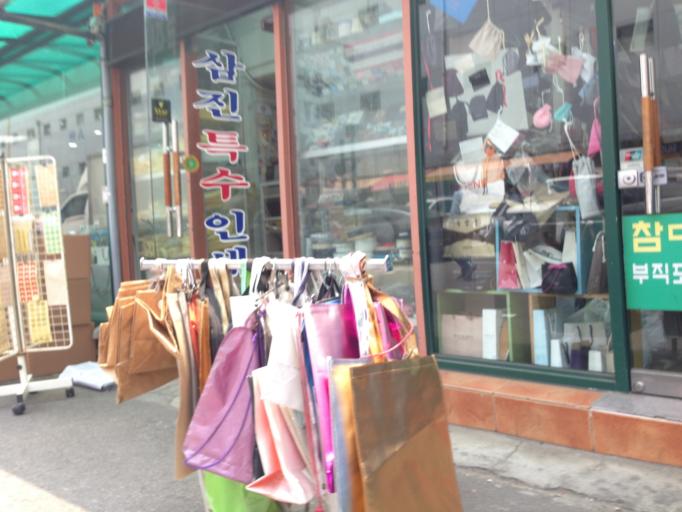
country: KR
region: Seoul
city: Seoul
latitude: 37.5684
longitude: 127.0003
